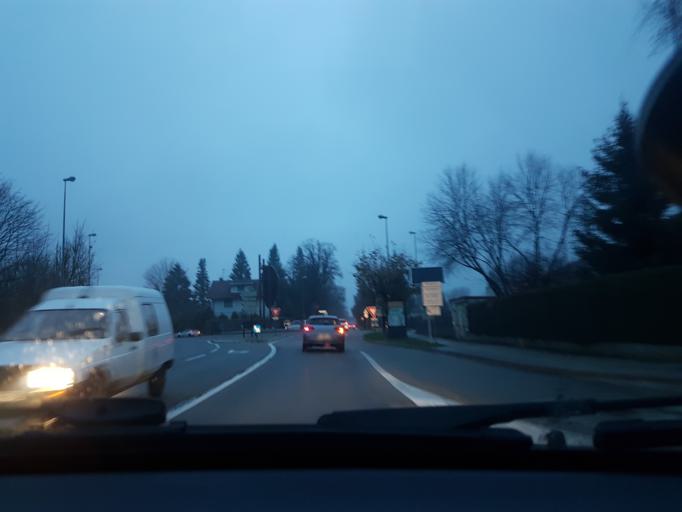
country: FR
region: Franche-Comte
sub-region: Departement du Doubs
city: Pontarlier
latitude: 46.8942
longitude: 6.3645
